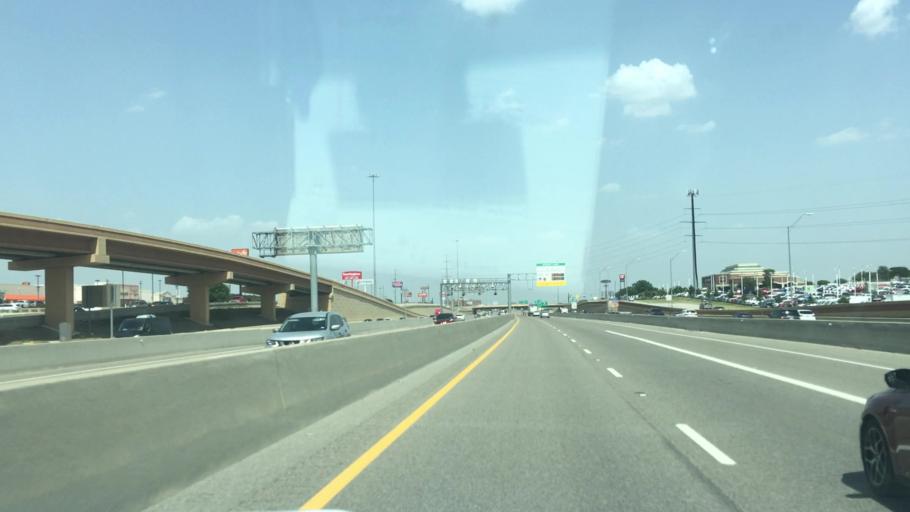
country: US
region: Texas
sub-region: Tarrant County
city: North Richland Hills
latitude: 32.8400
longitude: -97.2460
